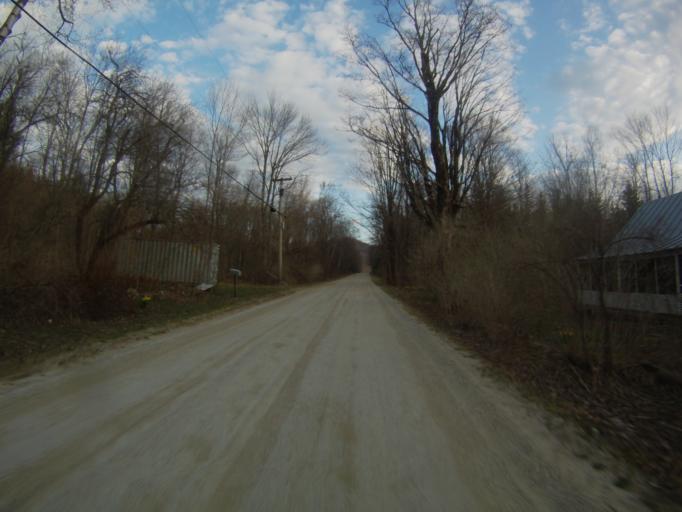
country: US
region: Vermont
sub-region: Rutland County
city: Brandon
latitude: 43.8536
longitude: -72.9988
